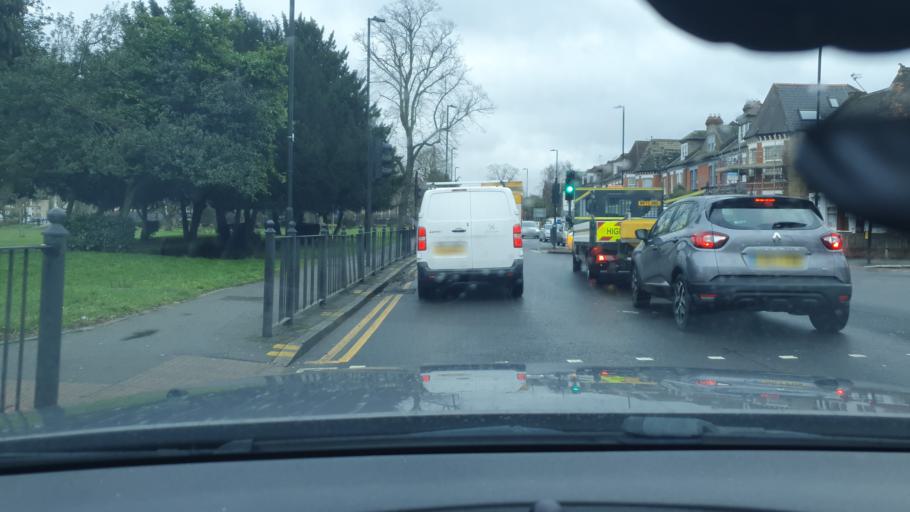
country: GB
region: England
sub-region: Greater London
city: Wood Green
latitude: 51.6007
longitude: -0.1160
